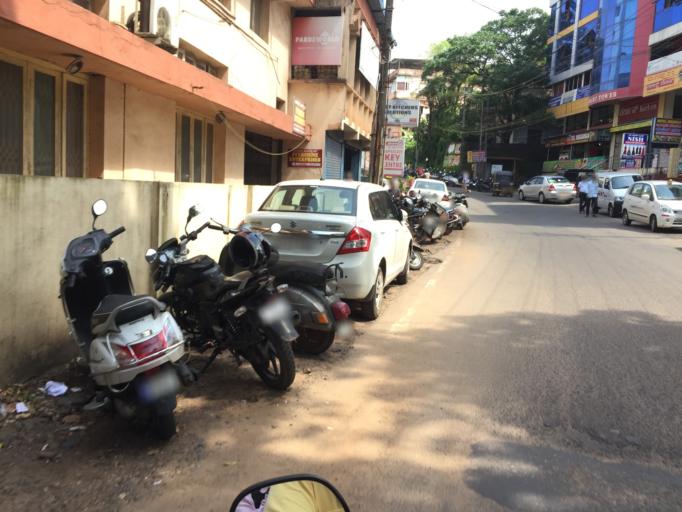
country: IN
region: Karnataka
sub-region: Dakshina Kannada
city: Mangalore
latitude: 12.8714
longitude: 74.8493
